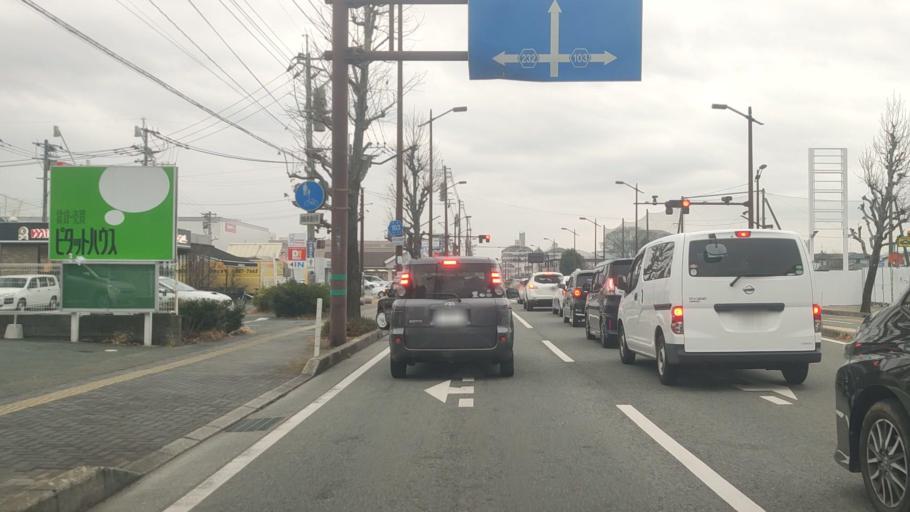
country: JP
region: Kumamoto
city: Kumamoto
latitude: 32.8102
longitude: 130.7712
